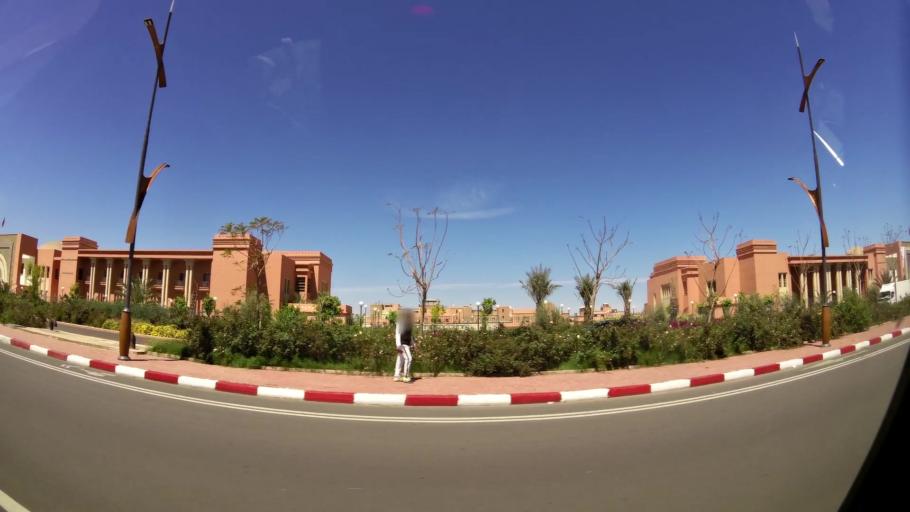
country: MA
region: Marrakech-Tensift-Al Haouz
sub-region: Marrakech
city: Marrakesh
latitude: 31.6116
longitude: -7.9940
